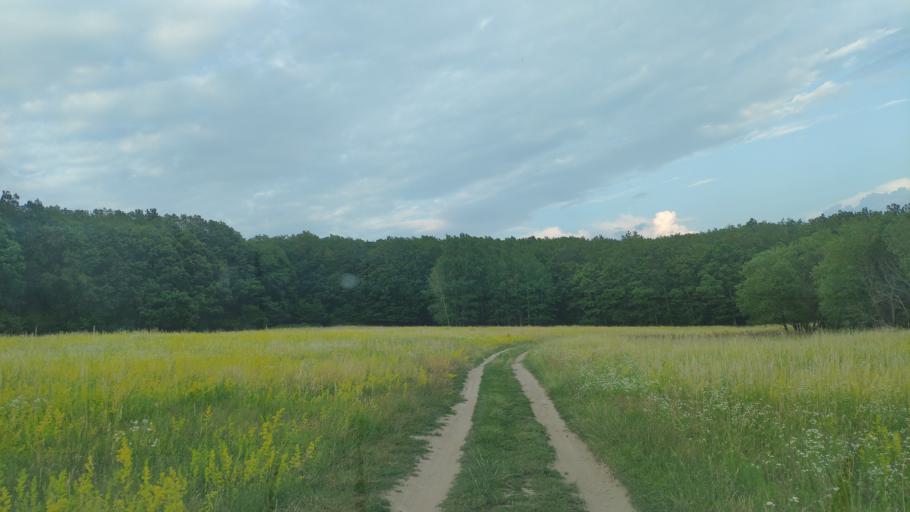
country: SK
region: Kosicky
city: Moldava nad Bodvou
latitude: 48.7186
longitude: 20.9989
